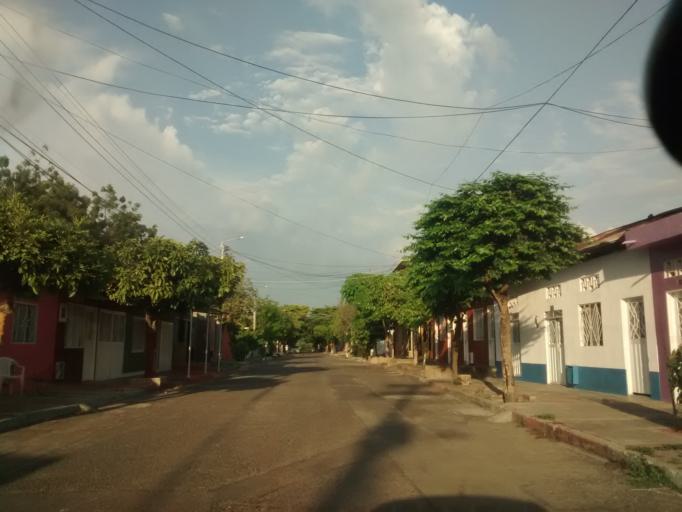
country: CO
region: Tolima
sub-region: Flandes
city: Flandes
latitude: 4.2958
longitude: -74.8187
